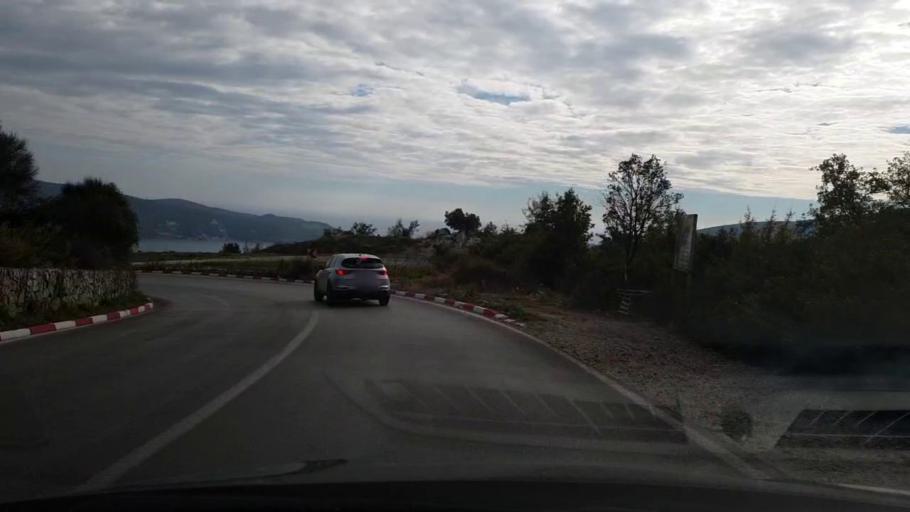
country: ME
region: Herceg Novi
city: Herceg-Novi
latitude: 42.4672
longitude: 18.5380
